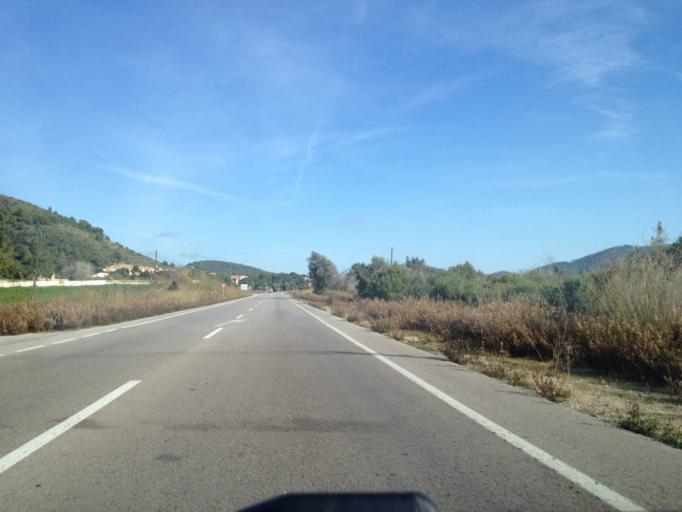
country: ES
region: Balearic Islands
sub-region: Illes Balears
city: Son Servera
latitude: 39.6400
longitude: 3.3712
